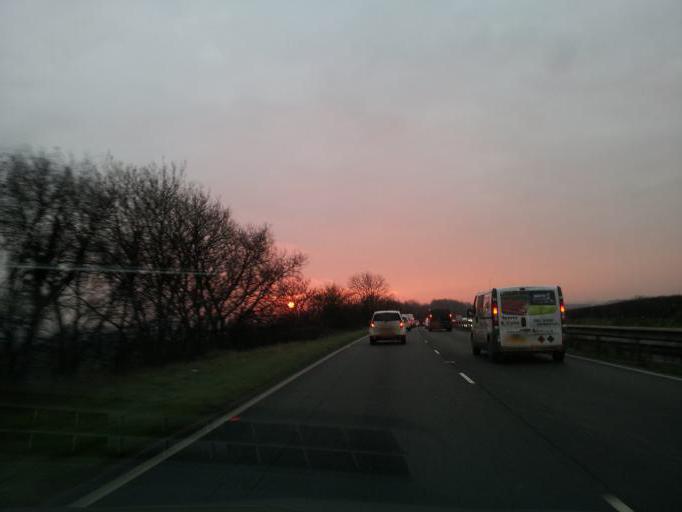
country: GB
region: England
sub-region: Peterborough
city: Thornhaugh
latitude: 52.6024
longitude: -0.4250
